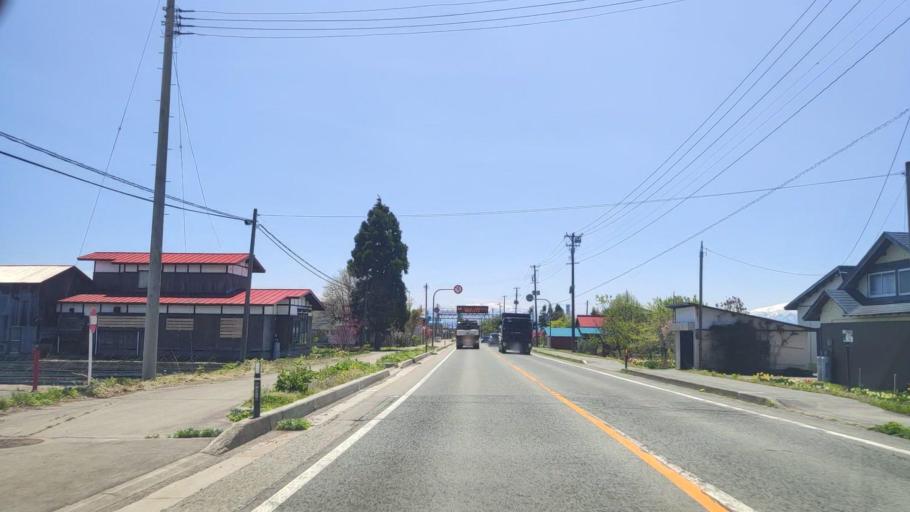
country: JP
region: Yamagata
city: Shinjo
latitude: 38.8191
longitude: 140.3261
